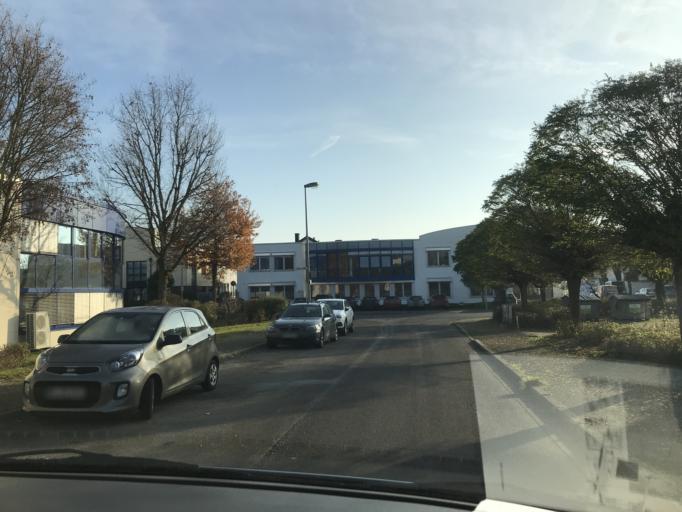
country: DE
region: North Rhine-Westphalia
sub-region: Regierungsbezirk Dusseldorf
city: Krefeld
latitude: 51.3282
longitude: 6.6217
